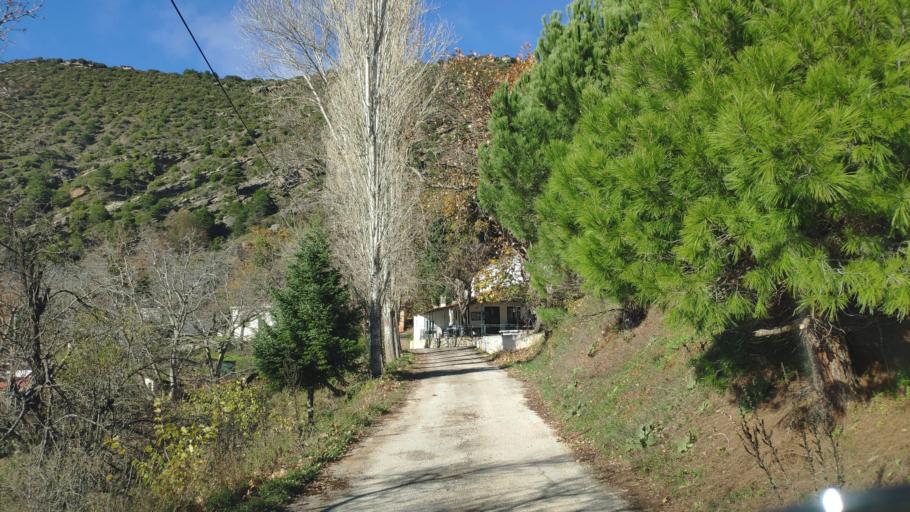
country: GR
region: West Greece
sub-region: Nomos Achaias
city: Aiyira
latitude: 38.0564
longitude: 22.4505
